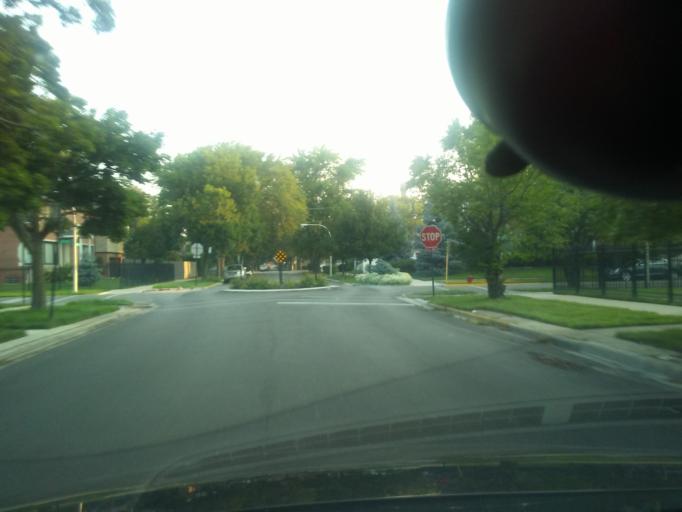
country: US
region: Illinois
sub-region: Cook County
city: Lincolnwood
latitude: 41.9819
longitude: -87.7016
